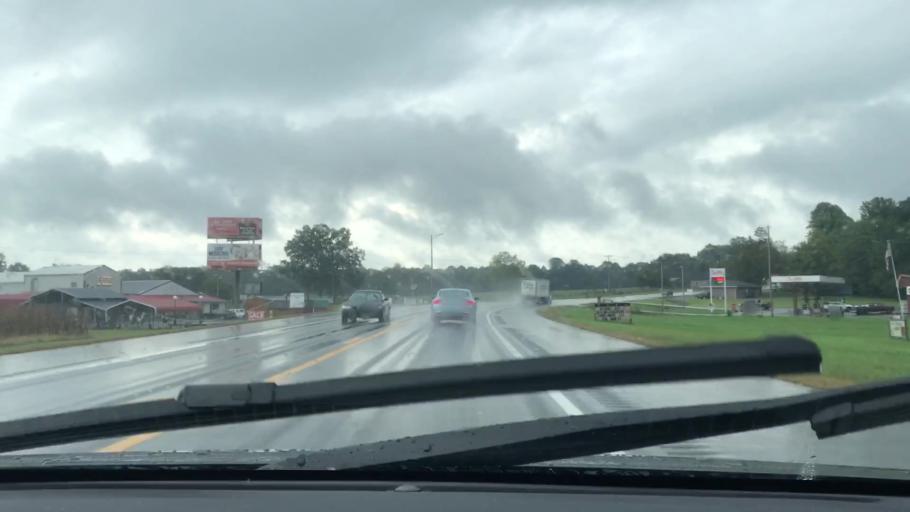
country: US
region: Tennessee
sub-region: Macon County
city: Lafayette
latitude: 36.5288
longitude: -86.0497
